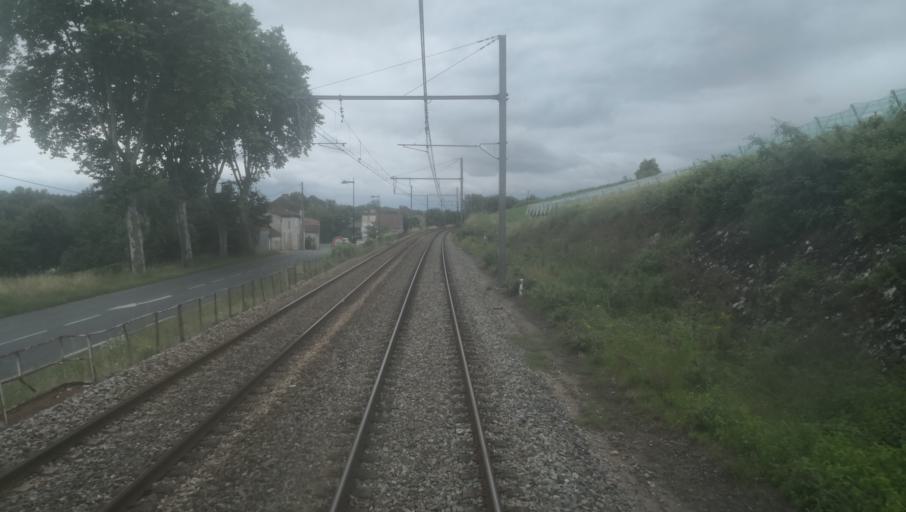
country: FR
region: Aquitaine
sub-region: Departement du Lot-et-Garonne
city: Port-Sainte-Marie
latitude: 44.2403
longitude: 0.4516
